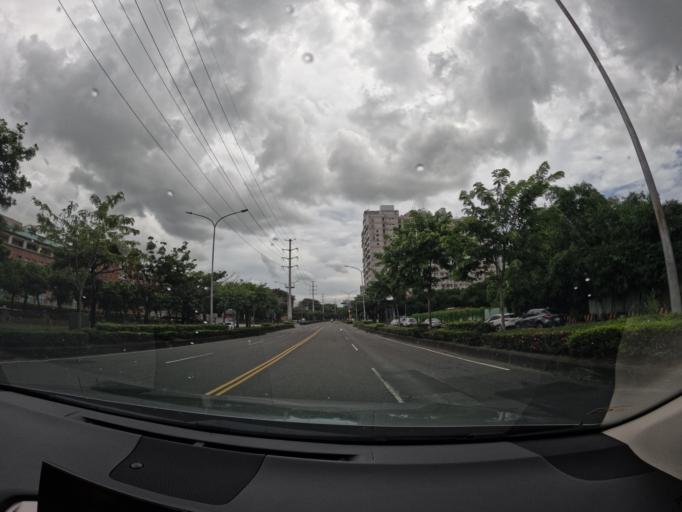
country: TW
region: Kaohsiung
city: Kaohsiung
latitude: 22.7292
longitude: 120.3136
